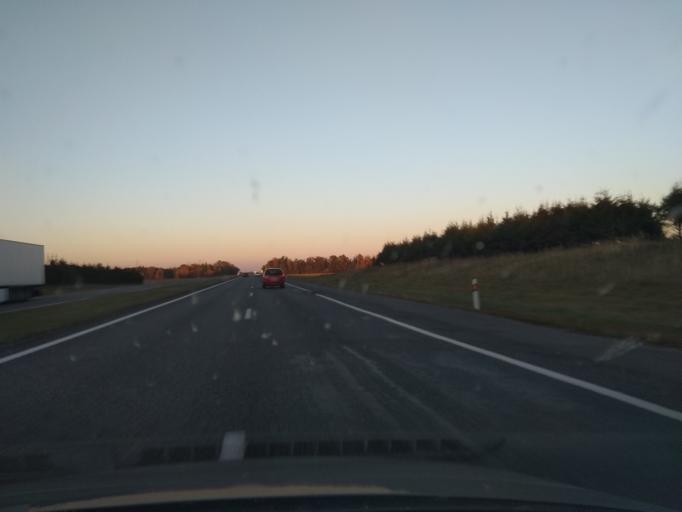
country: BY
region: Minsk
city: Haradzyeya
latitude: 53.3724
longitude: 26.4952
